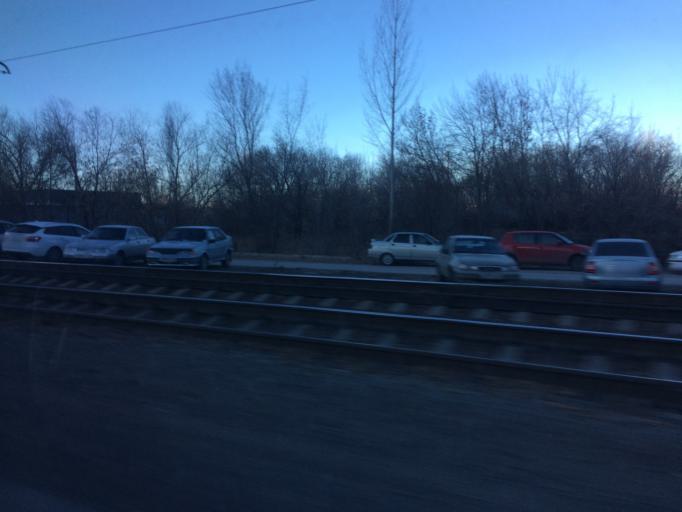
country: RU
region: Chelyabinsk
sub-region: Gorod Magnitogorsk
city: Magnitogorsk
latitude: 53.4009
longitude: 59.0253
